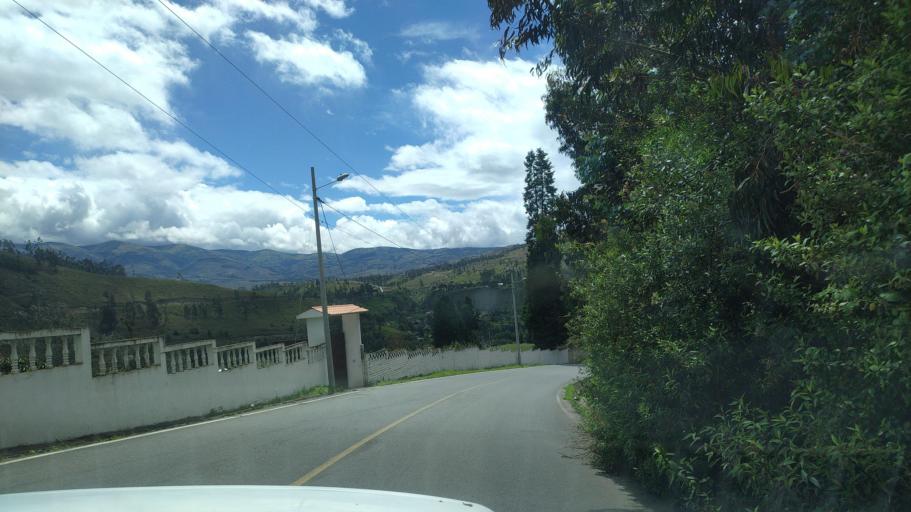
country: EC
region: Chimborazo
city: Riobamba
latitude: -1.6593
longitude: -78.5841
